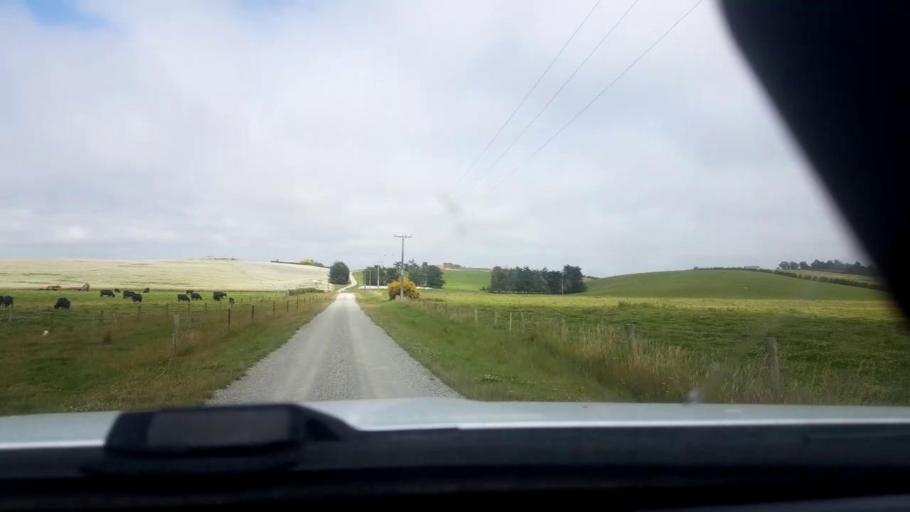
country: NZ
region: Canterbury
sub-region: Timaru District
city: Timaru
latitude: -44.3291
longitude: 171.2034
